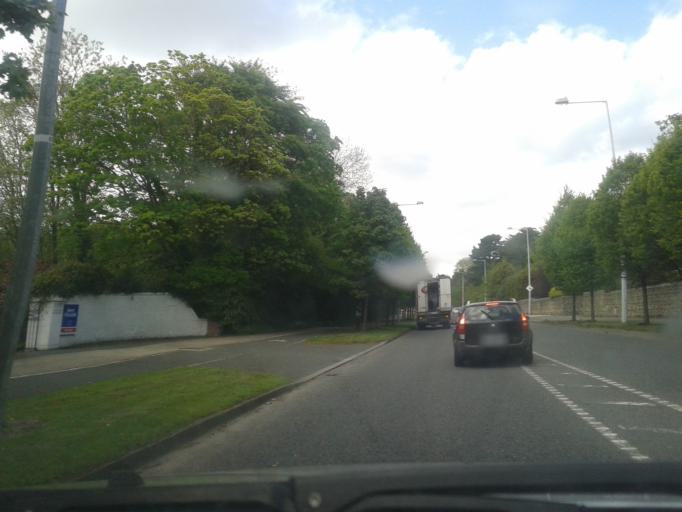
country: IE
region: Leinster
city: Loughlinstown
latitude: 53.2597
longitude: -6.1290
